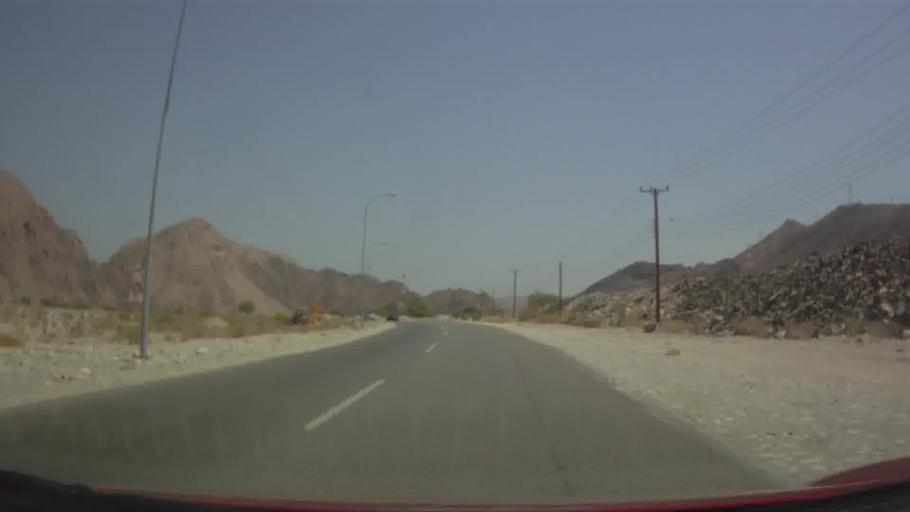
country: OM
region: Muhafazat Masqat
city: Muscat
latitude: 23.5097
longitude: 58.6380
